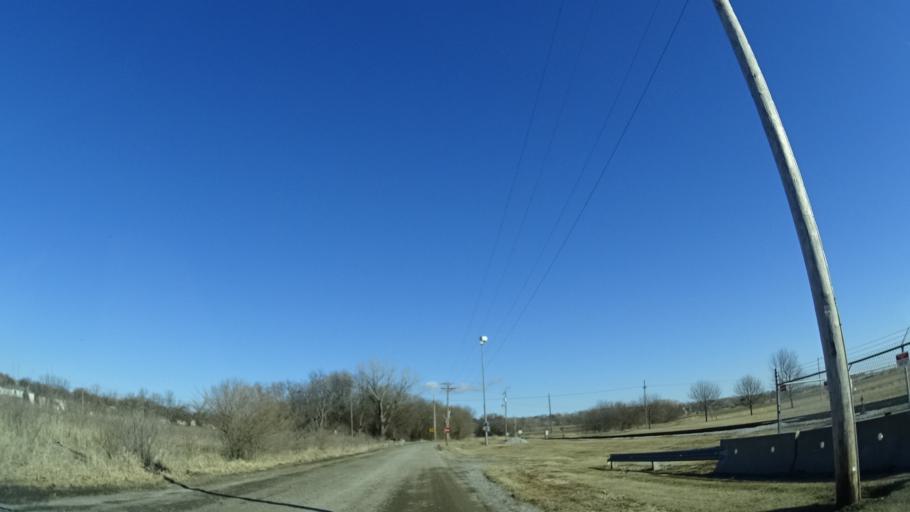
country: US
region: Nebraska
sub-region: Sarpy County
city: Offutt Air Force Base
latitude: 41.1473
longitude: -95.9491
